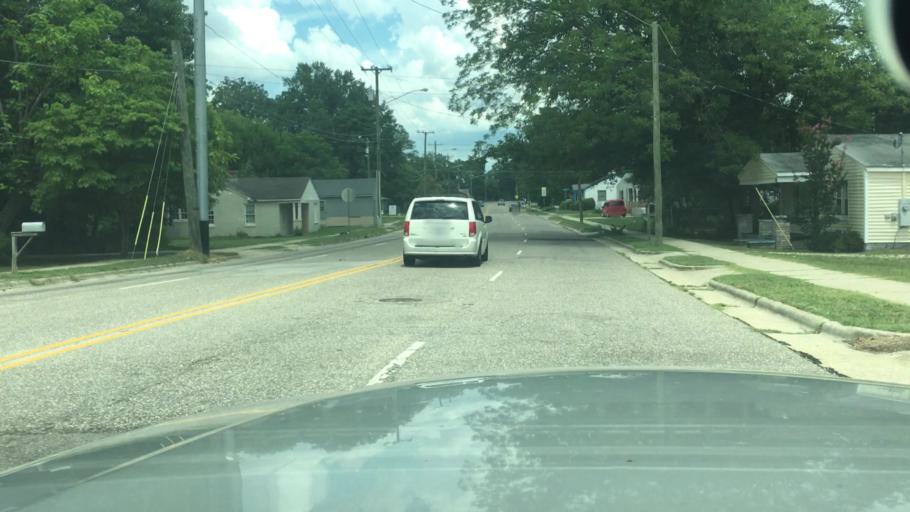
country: US
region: North Carolina
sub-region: Cumberland County
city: Fayetteville
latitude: 35.0860
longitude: -78.9024
